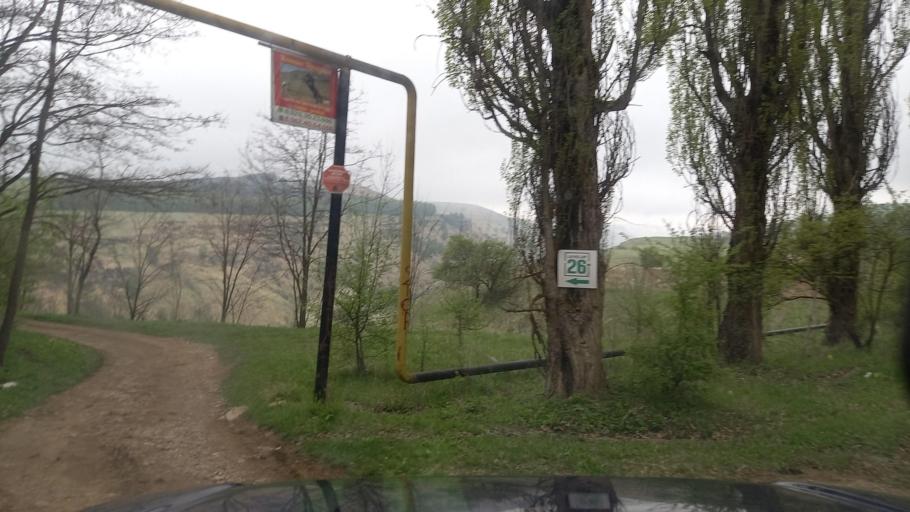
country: RU
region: Stavropol'skiy
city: Nezhinskiy
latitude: 43.8799
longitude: 42.6814
